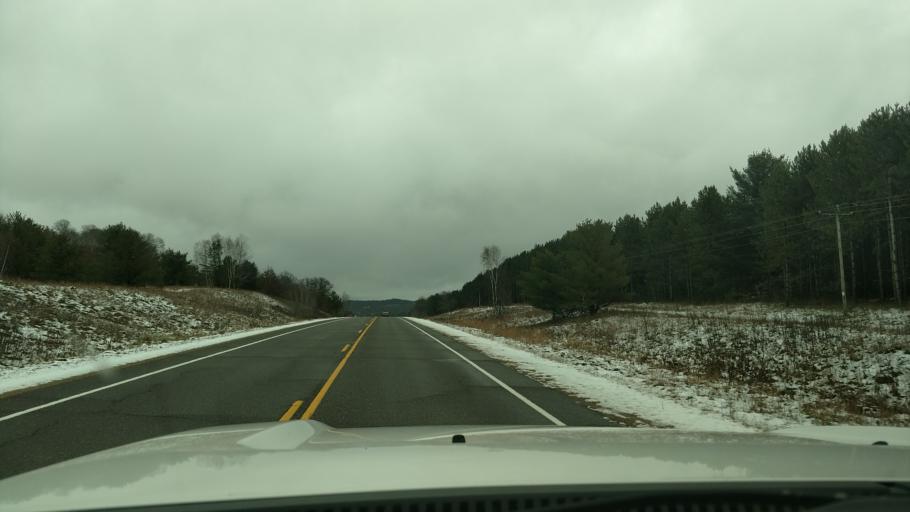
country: US
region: Wisconsin
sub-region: Dunn County
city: Tainter Lake
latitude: 45.1239
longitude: -91.8699
